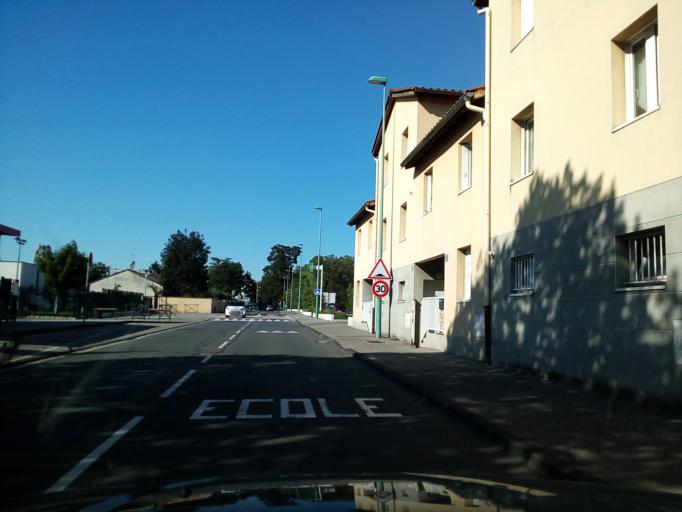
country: FR
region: Rhone-Alpes
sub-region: Departement du Rhone
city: Vaulx-en-Velin
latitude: 45.7855
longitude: 4.9172
